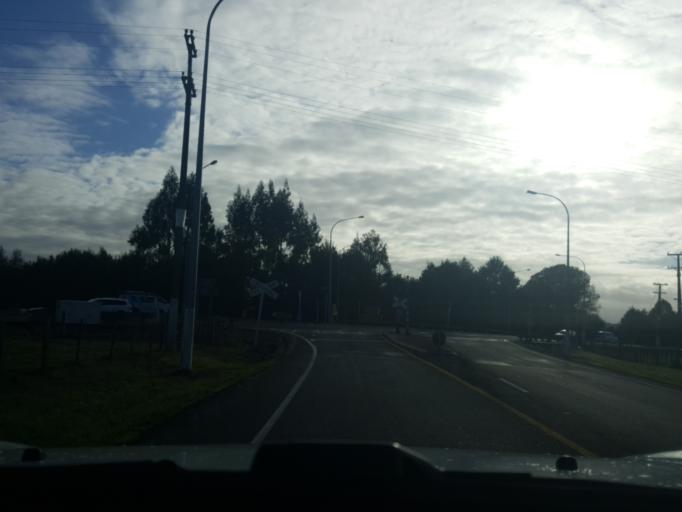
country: NZ
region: Waikato
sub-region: Waipa District
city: Cambridge
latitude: -37.6690
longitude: 175.4836
